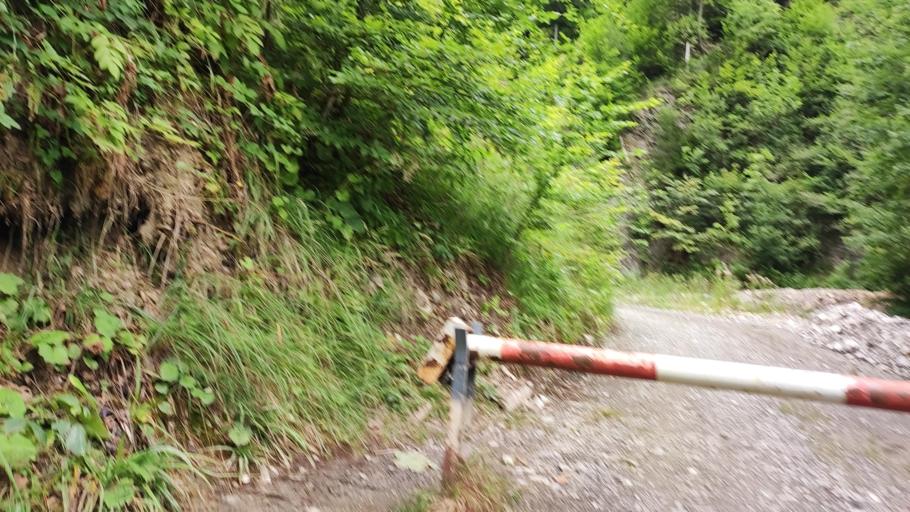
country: AT
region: Vorarlberg
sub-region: Politischer Bezirk Feldkirch
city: Feldkirch
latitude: 47.1992
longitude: 9.6058
